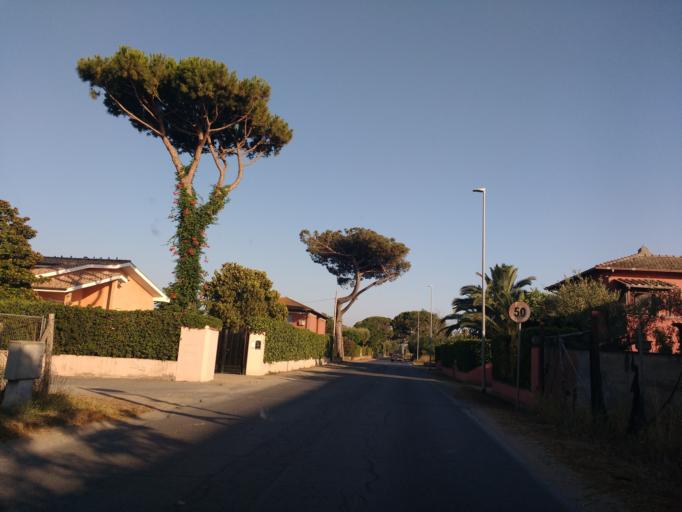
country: IT
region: Latium
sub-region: Citta metropolitana di Roma Capitale
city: Fregene
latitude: 41.8462
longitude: 12.2217
